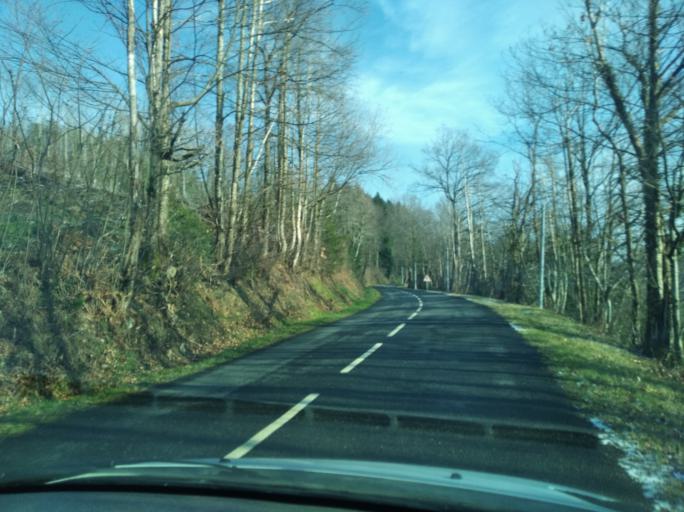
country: FR
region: Auvergne
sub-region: Departement de l'Allier
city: Le Mayet-de-Montagne
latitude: 46.1471
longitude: 3.7397
